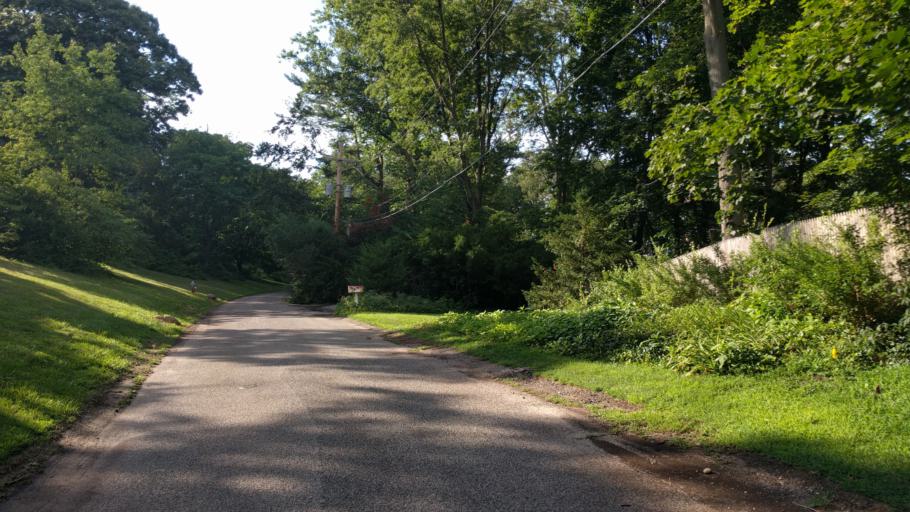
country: US
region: New York
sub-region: Nassau County
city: Oyster Bay Cove
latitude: 40.8719
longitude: -73.5097
